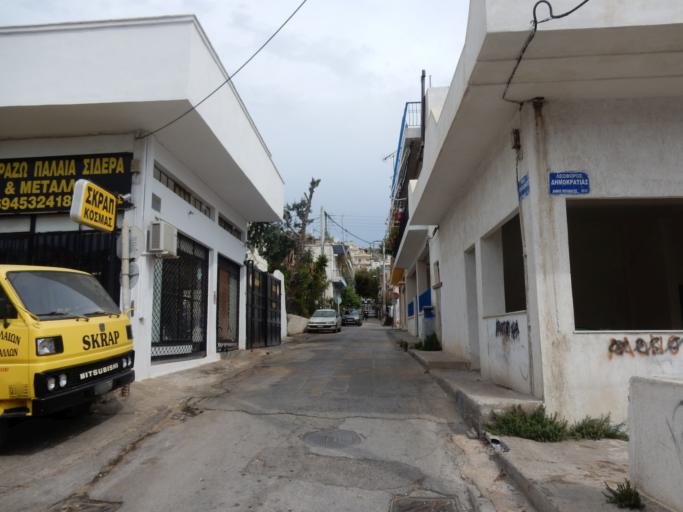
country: GR
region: Attica
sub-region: Nomos Piraios
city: Perama
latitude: 37.9633
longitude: 23.5684
